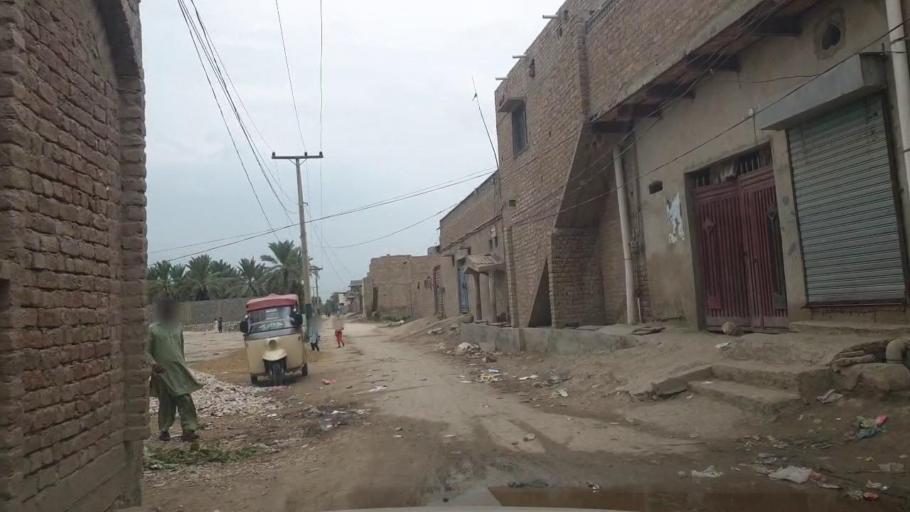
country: PK
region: Sindh
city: Khairpur
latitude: 27.5431
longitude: 68.7399
